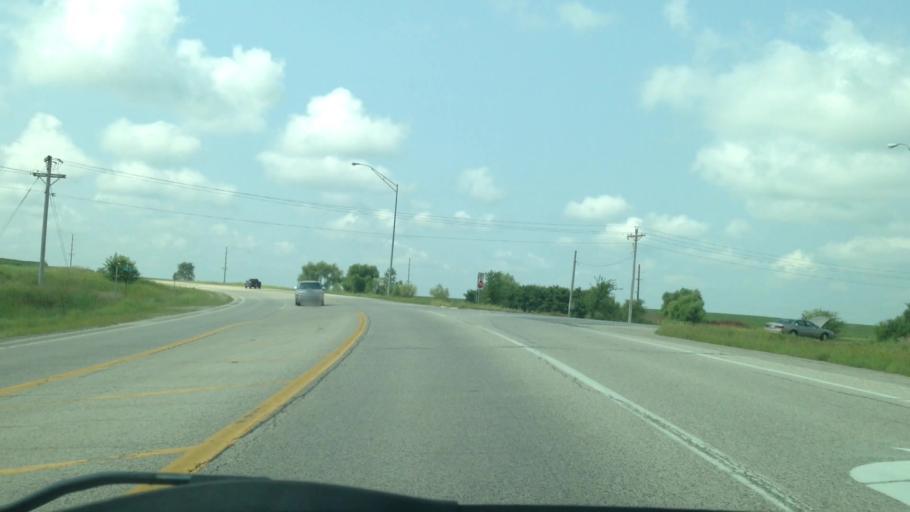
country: US
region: Iowa
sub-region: Benton County
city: Walford
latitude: 41.8757
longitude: -91.8671
